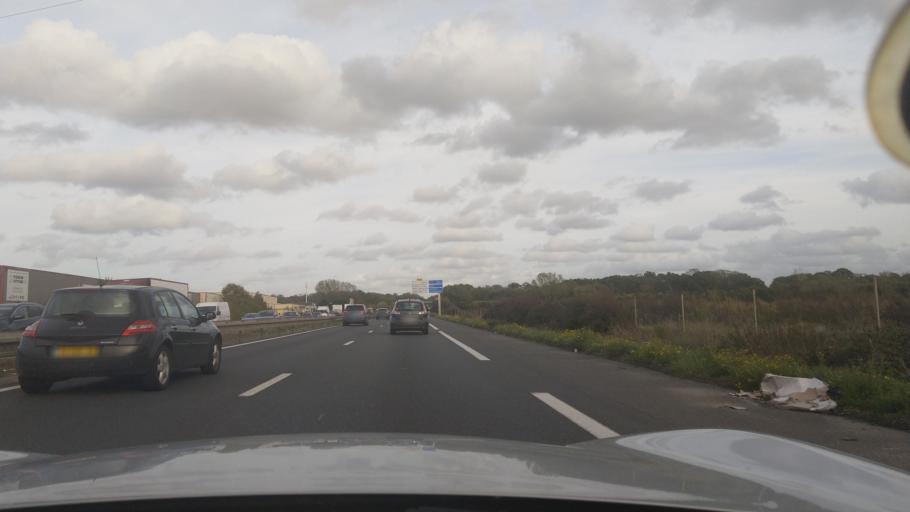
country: FR
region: Ile-de-France
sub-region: Departement du Val-d'Oise
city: Auvers-sur-Oise
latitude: 49.0527
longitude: 2.1639
